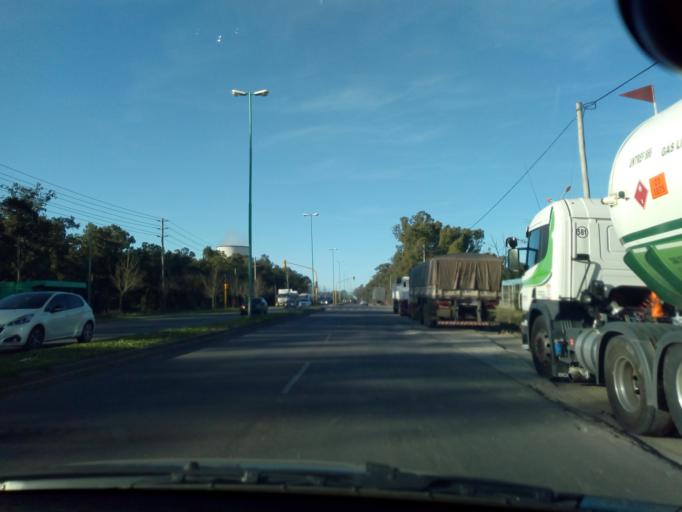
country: AR
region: Buenos Aires
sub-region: Partido de Ensenada
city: Ensenada
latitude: -34.8849
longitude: -57.9283
